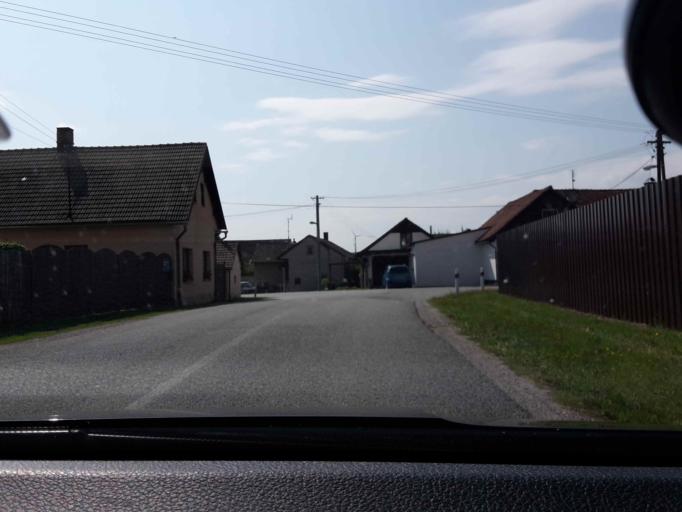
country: CZ
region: Vysocina
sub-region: Okres Jihlava
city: Trest'
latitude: 49.2665
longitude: 15.5711
